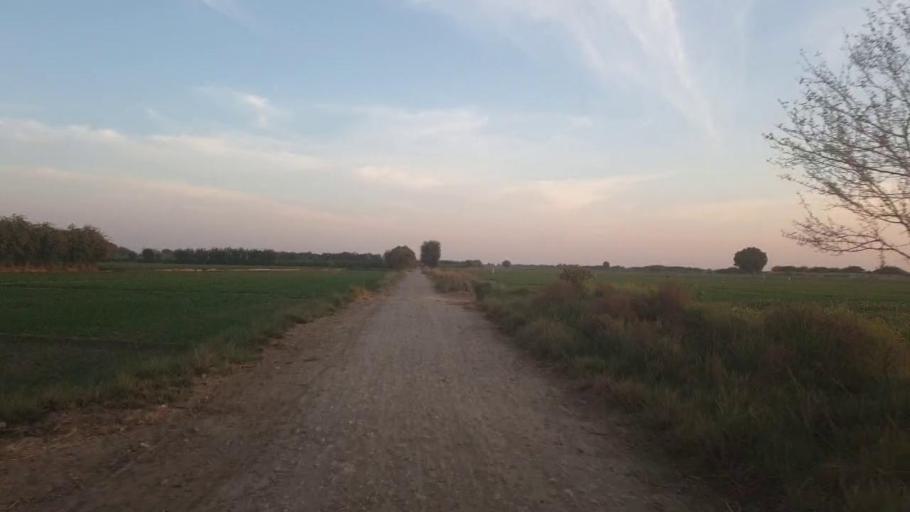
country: PK
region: Sindh
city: Hala
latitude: 25.6988
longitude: 68.3172
